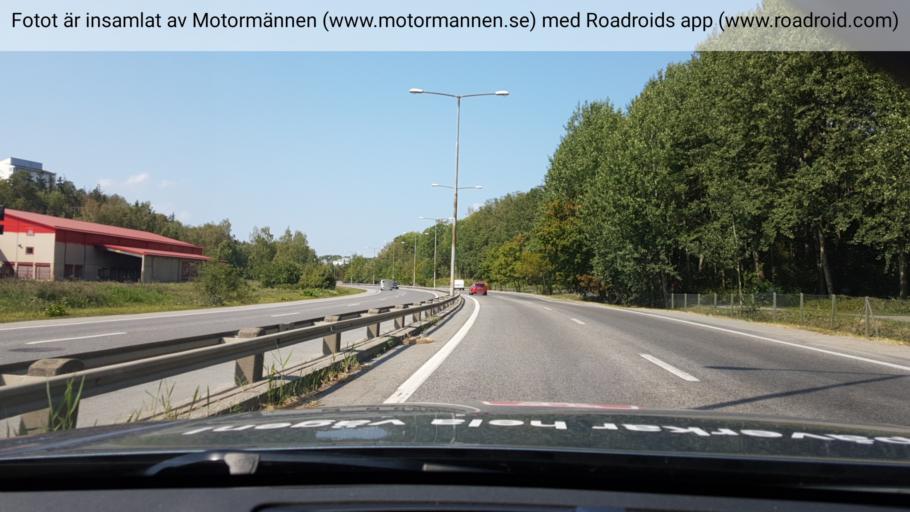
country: SE
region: Stockholm
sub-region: Stockholms Kommun
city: Arsta
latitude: 59.2613
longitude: 18.0344
